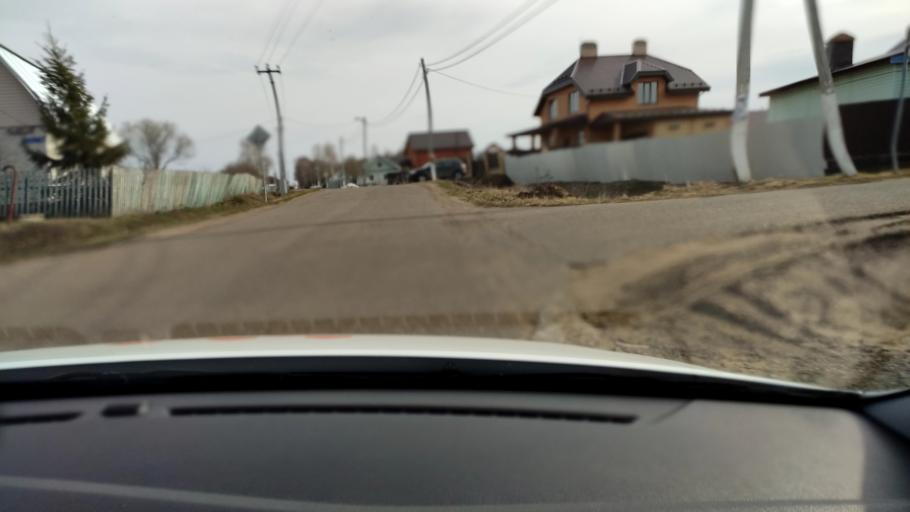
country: RU
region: Tatarstan
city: Stolbishchi
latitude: 55.6471
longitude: 49.3101
